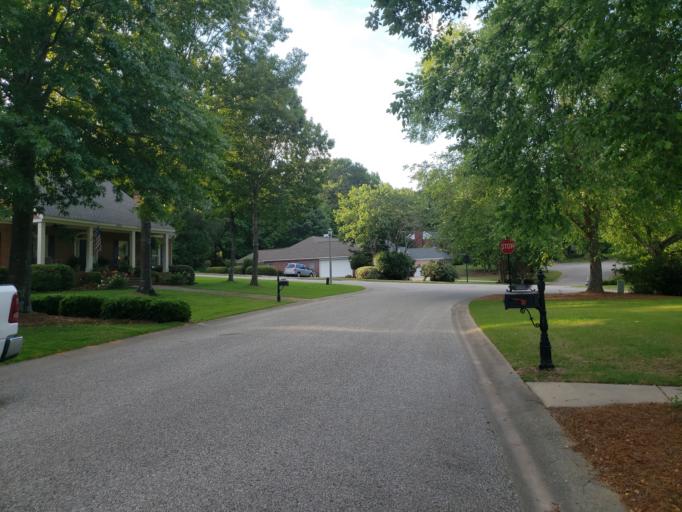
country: US
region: Alabama
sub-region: Lee County
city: Auburn
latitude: 32.5840
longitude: -85.4563
